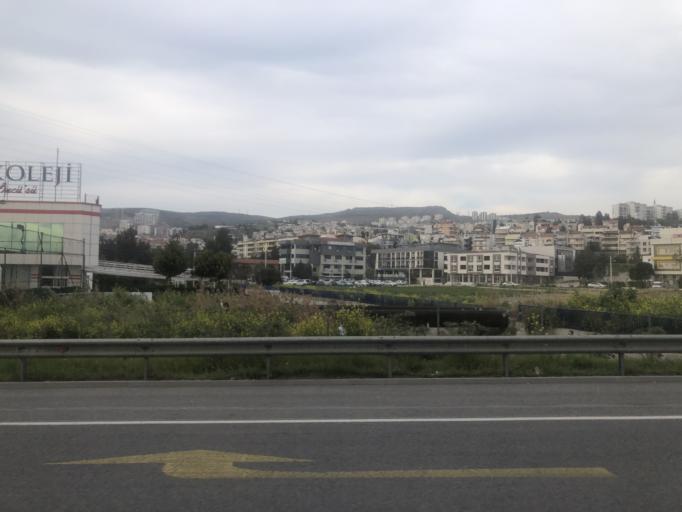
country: TR
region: Izmir
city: Karsiyaka
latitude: 38.4870
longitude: 27.0767
